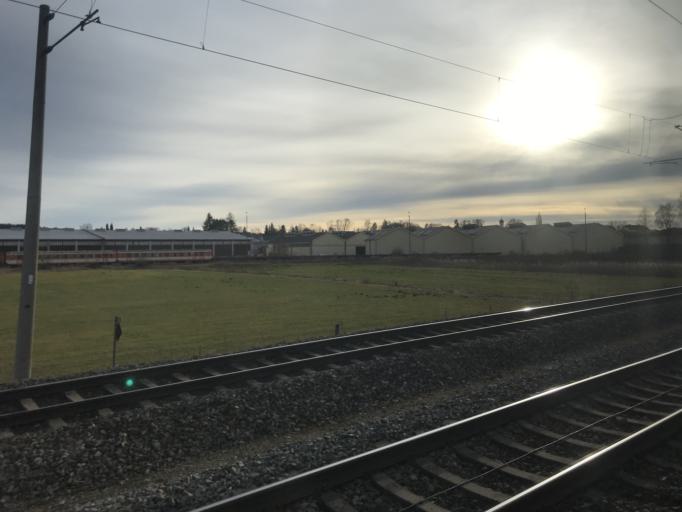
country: DE
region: Bavaria
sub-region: Swabia
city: Gessertshausen
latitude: 48.3347
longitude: 10.7381
